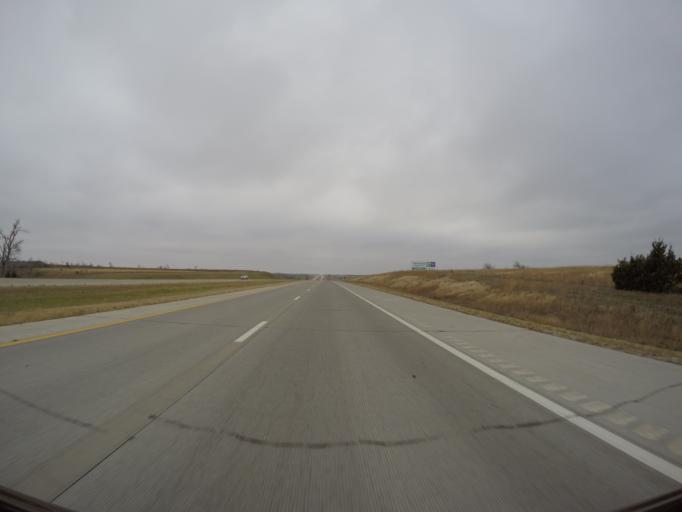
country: US
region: Kansas
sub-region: Dickinson County
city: Chapman
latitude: 38.9692
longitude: -97.0838
